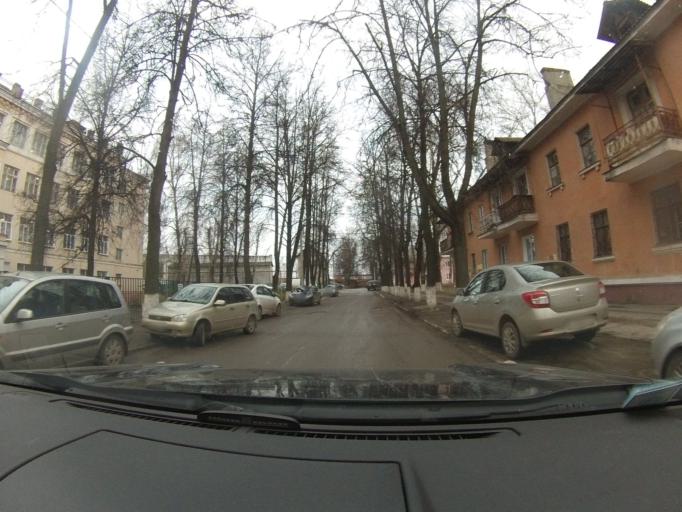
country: RU
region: Moskovskaya
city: Voskresensk
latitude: 55.3227
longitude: 38.6839
